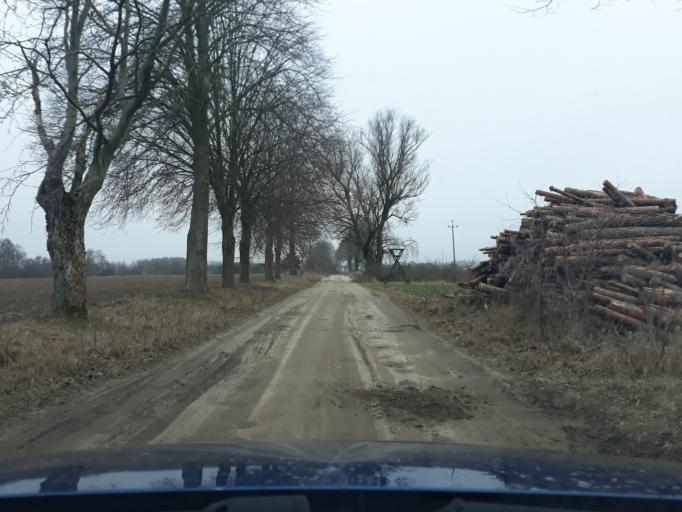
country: PL
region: Pomeranian Voivodeship
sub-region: Powiat czluchowski
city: Czluchow
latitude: 53.8187
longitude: 17.4116
